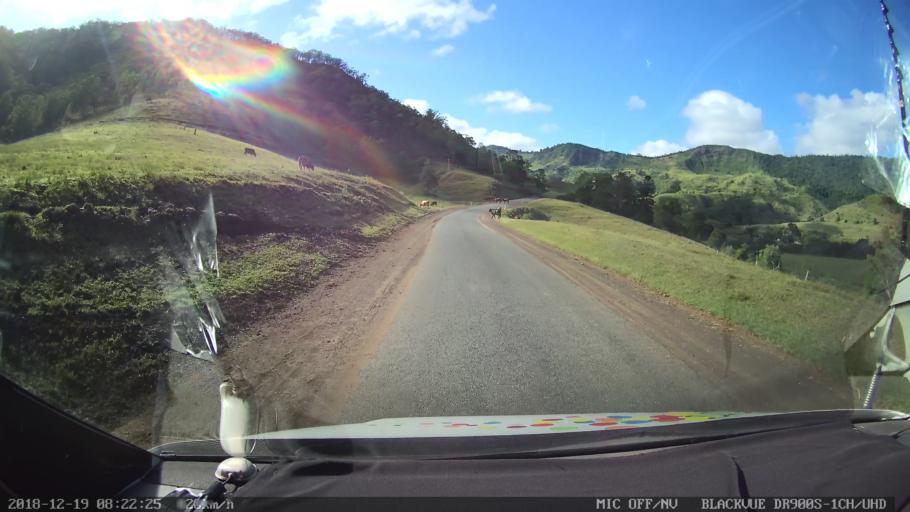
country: AU
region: New South Wales
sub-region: Kyogle
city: Kyogle
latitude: -28.3034
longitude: 152.9112
